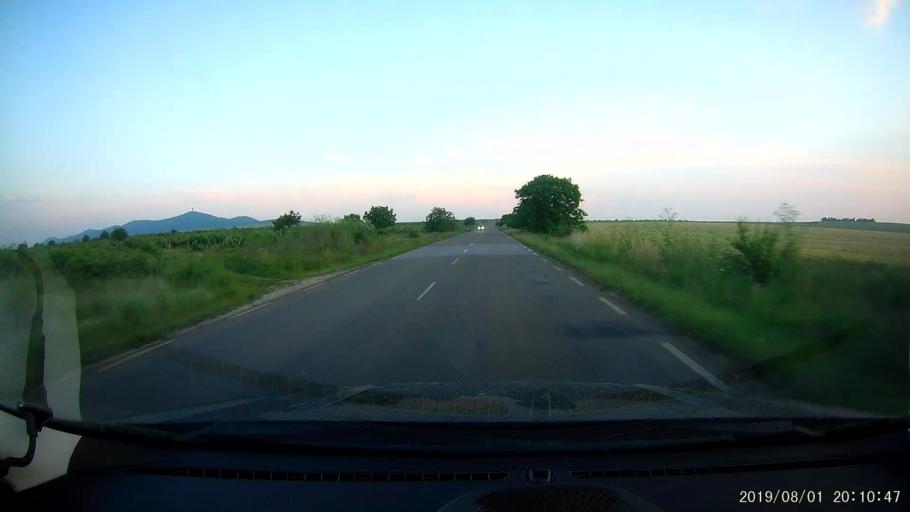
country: BG
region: Yambol
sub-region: Obshtina Yambol
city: Yambol
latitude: 42.4747
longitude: 26.6026
